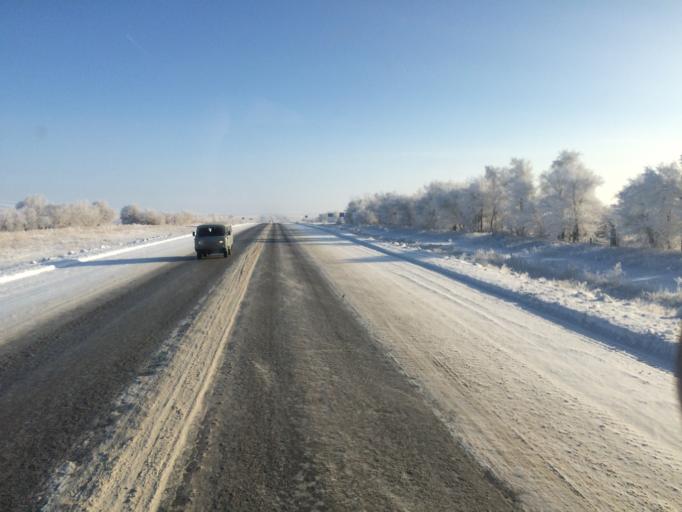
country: KZ
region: Aqtoebe
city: Martuk
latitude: 50.1865
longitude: 55.8124
